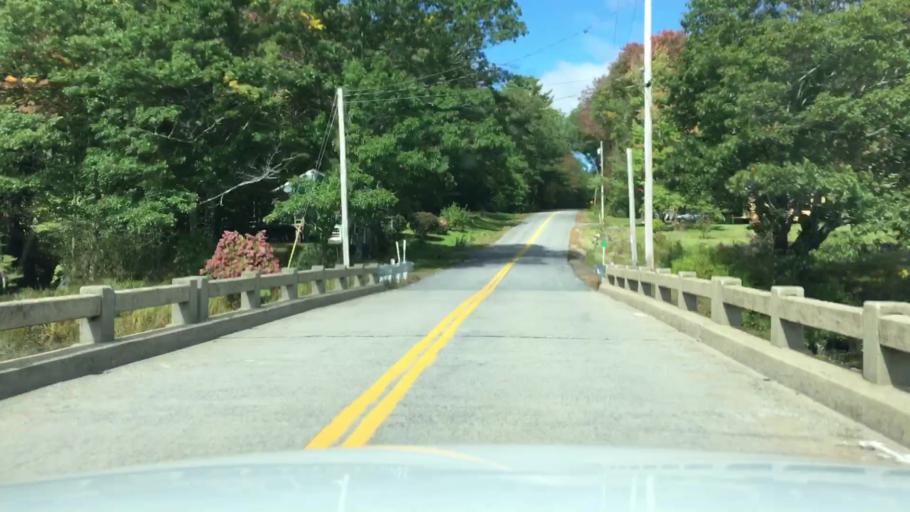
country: US
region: Maine
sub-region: Cumberland County
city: Brunswick
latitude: 43.9654
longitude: -69.8971
